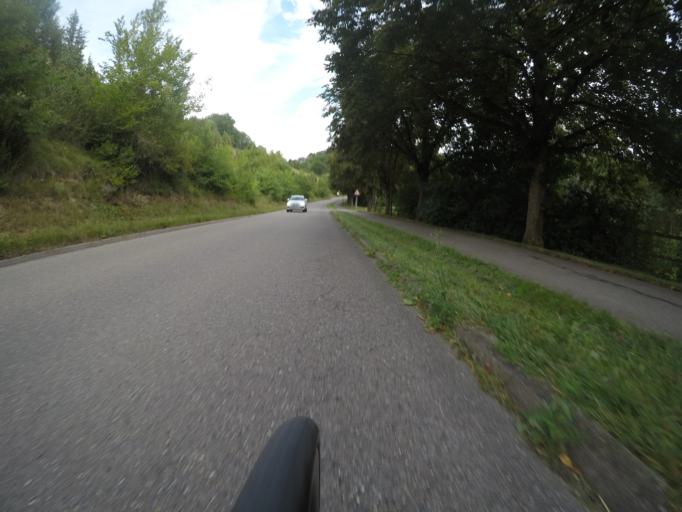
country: DE
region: Baden-Wuerttemberg
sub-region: Regierungsbezirk Stuttgart
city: Aidlingen
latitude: 48.7092
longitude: 8.9164
